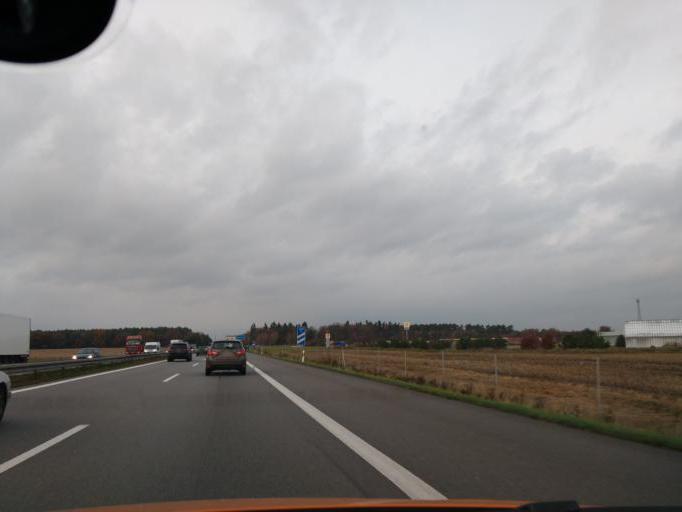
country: DE
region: Brandenburg
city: Wittstock
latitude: 53.0639
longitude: 12.5314
